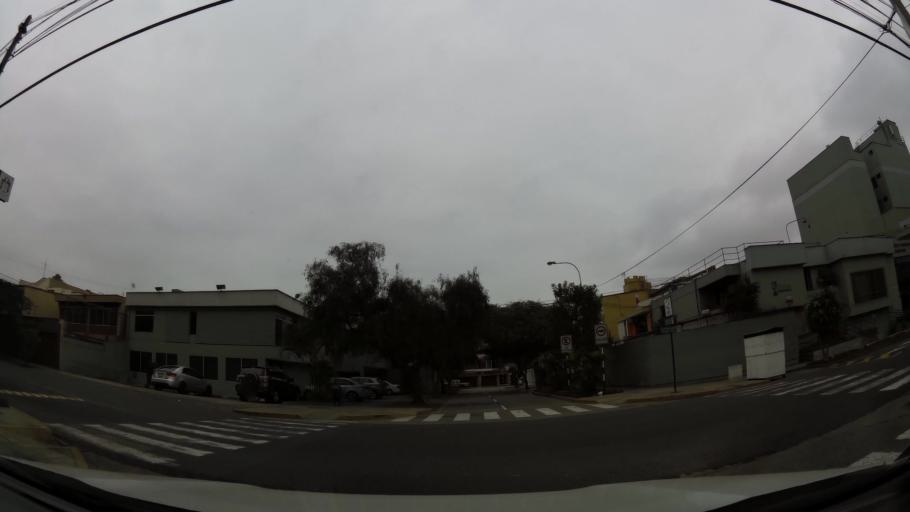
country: PE
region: Lima
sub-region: Lima
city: San Luis
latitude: -12.0909
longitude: -77.0175
